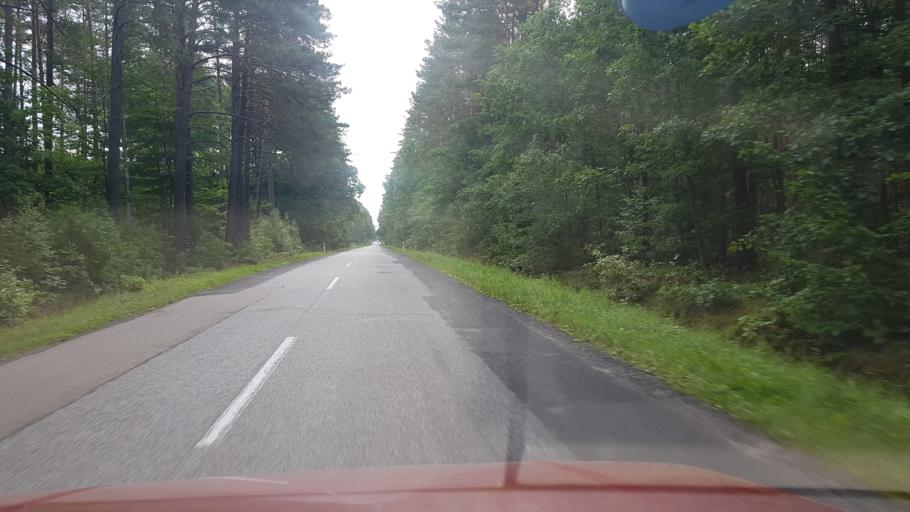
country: PL
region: West Pomeranian Voivodeship
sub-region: Powiat koszalinski
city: Polanow
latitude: 54.1040
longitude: 16.8021
